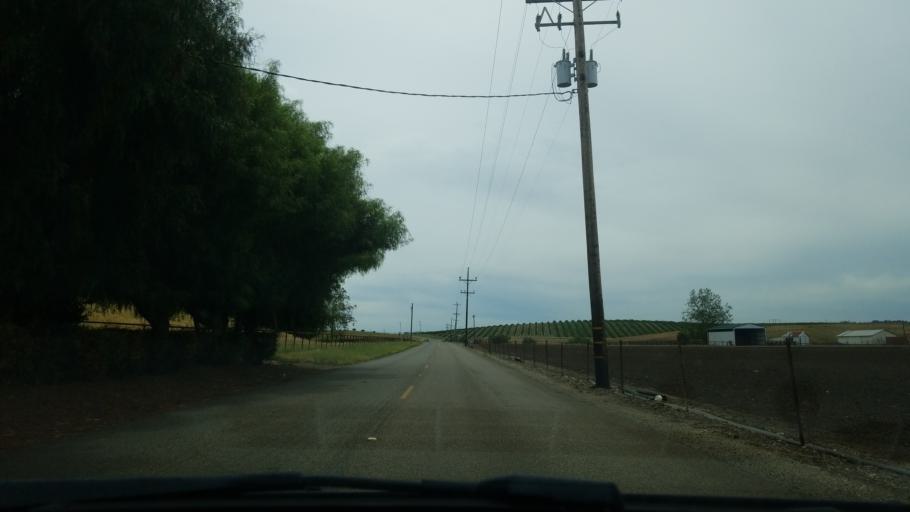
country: US
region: California
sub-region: San Luis Obispo County
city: Pismo Beach
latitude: 35.2127
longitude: -120.5898
